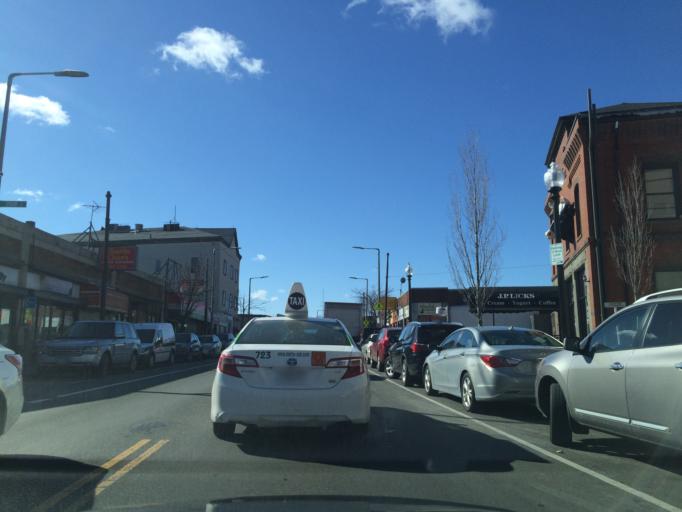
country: US
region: Massachusetts
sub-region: Suffolk County
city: Jamaica Plain
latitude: 42.3131
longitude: -71.1141
